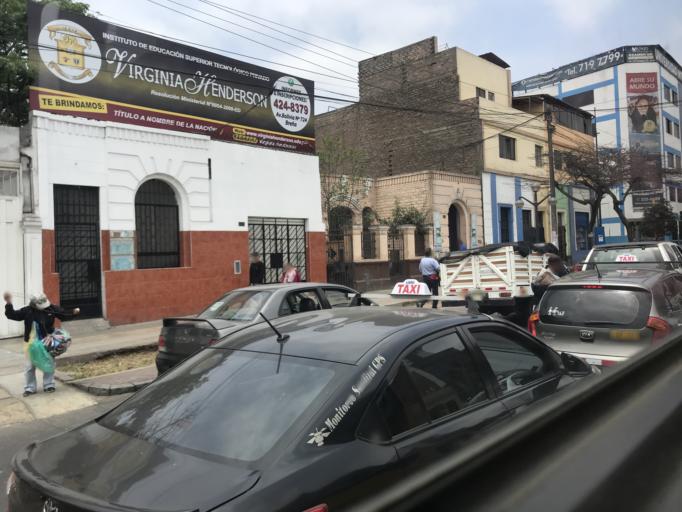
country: PE
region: Lima
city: Lima
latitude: -12.0566
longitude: -77.0458
